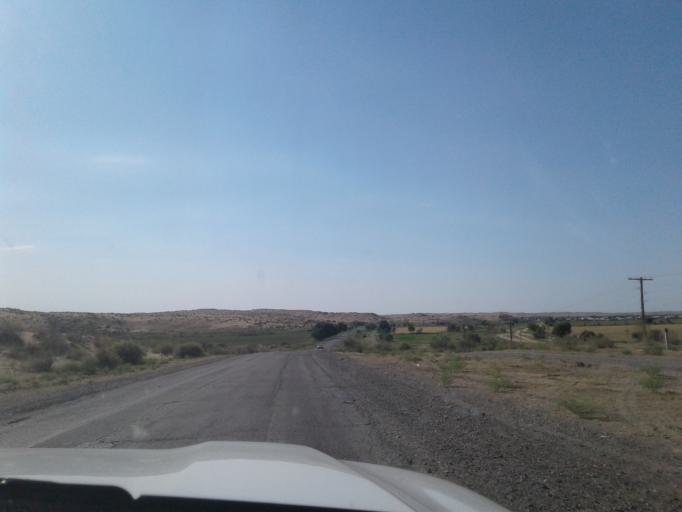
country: TM
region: Mary
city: Yoloeten
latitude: 36.6794
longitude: 62.4737
